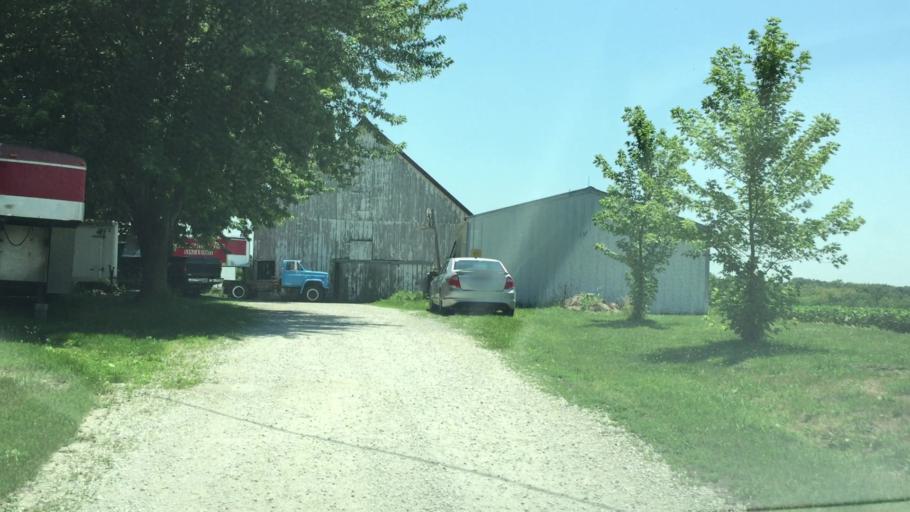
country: US
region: Illinois
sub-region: Hancock County
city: Carthage
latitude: 40.3277
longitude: -91.1693
